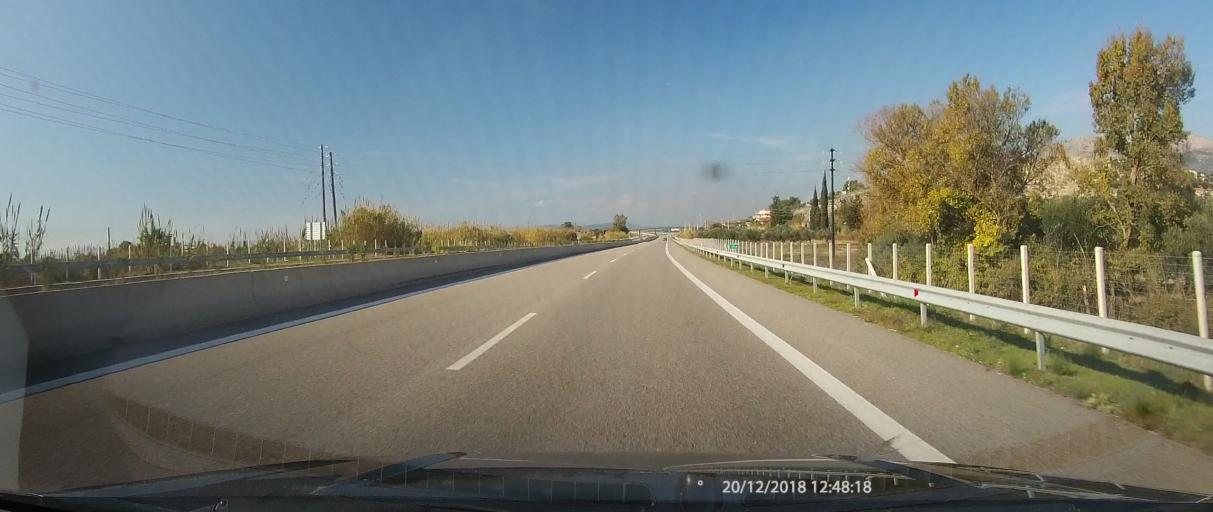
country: GR
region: West Greece
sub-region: Nomos Aitolias kai Akarnanias
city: Mesolongi
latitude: 38.3947
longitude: 21.4226
